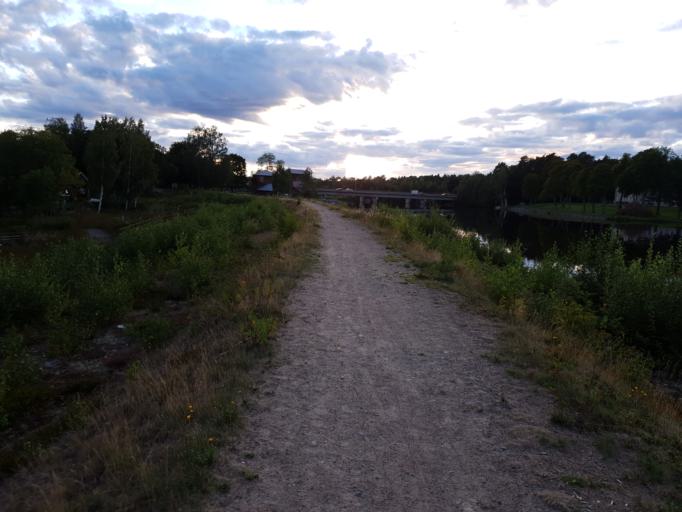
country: SE
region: Gaevleborg
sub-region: Soderhamns Kommun
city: Ljusne
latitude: 61.2061
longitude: 17.1185
